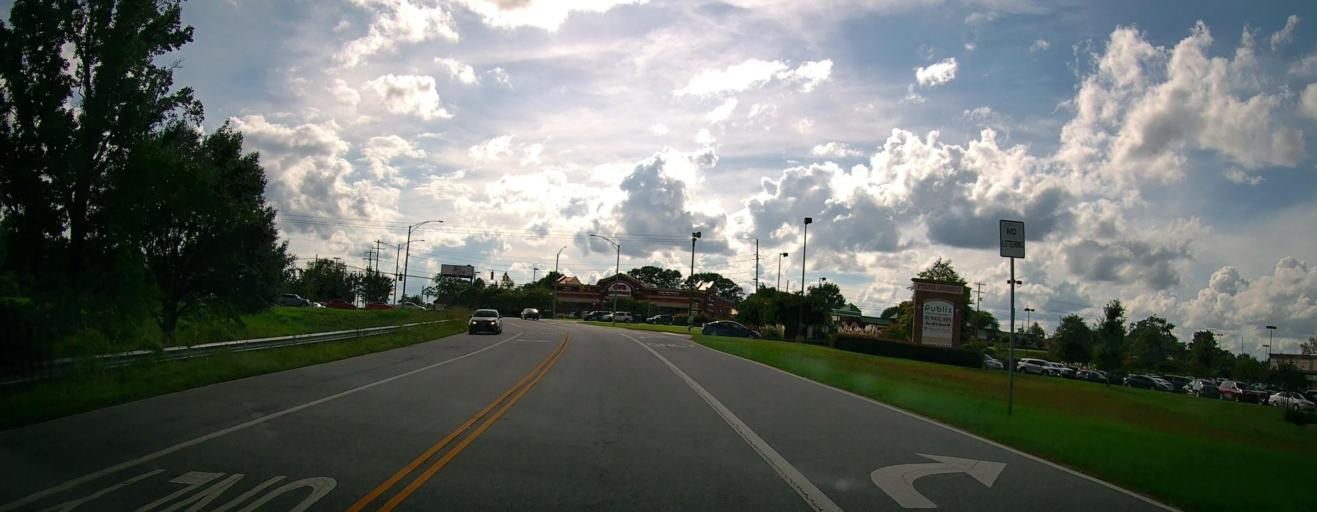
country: US
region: Alabama
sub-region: Russell County
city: Phenix City
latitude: 32.5203
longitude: -85.0271
